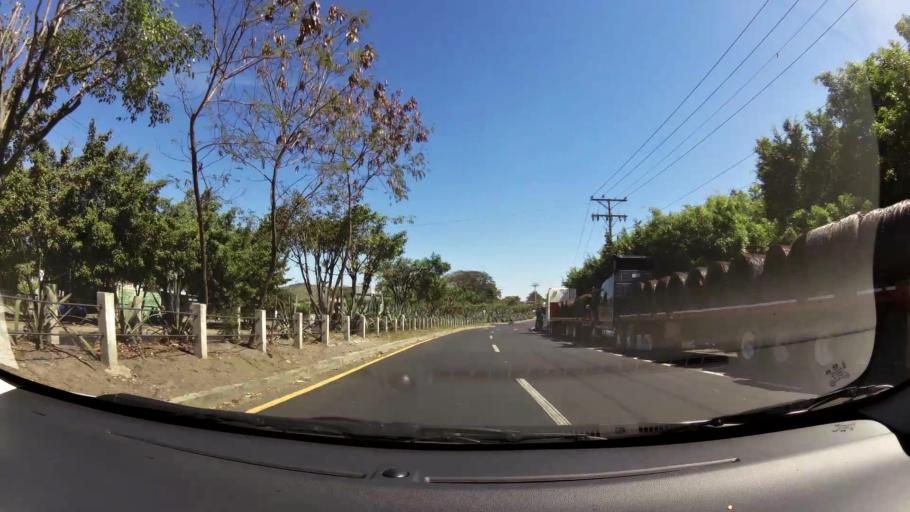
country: SV
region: La Libertad
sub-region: Distrito de Quezaltepeque
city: Quezaltepeque
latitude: 13.8271
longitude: -89.2660
